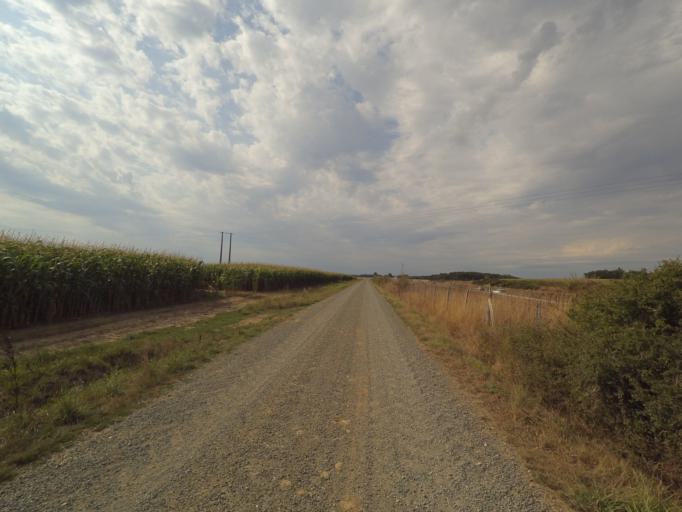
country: FR
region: Pays de la Loire
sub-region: Departement de la Vendee
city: Bouffere
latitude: 46.9755
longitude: -1.3705
